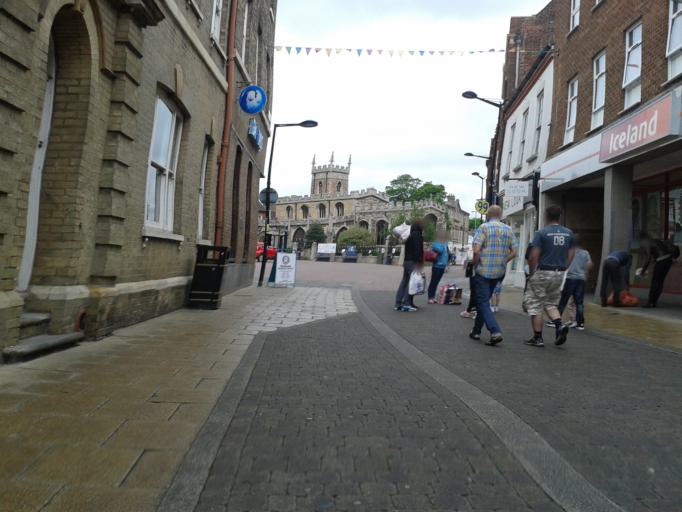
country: GB
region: England
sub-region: Cambridgeshire
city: Huntingdon
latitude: 52.3304
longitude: -0.1836
